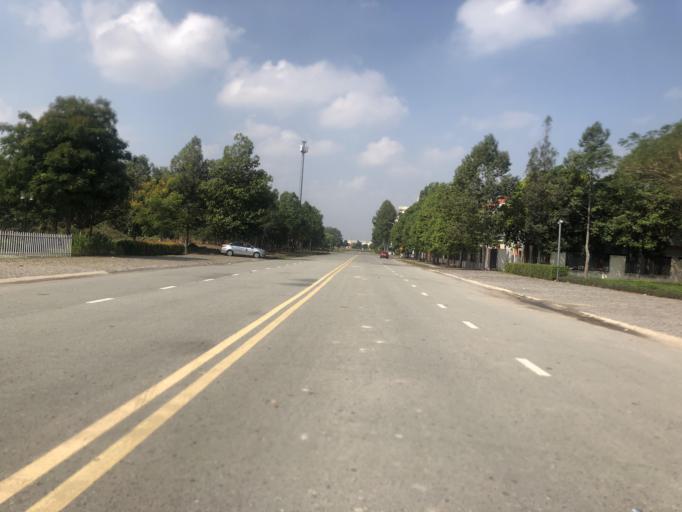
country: VN
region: Binh Duong
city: Thu Dau Mot
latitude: 11.0691
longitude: 106.6783
